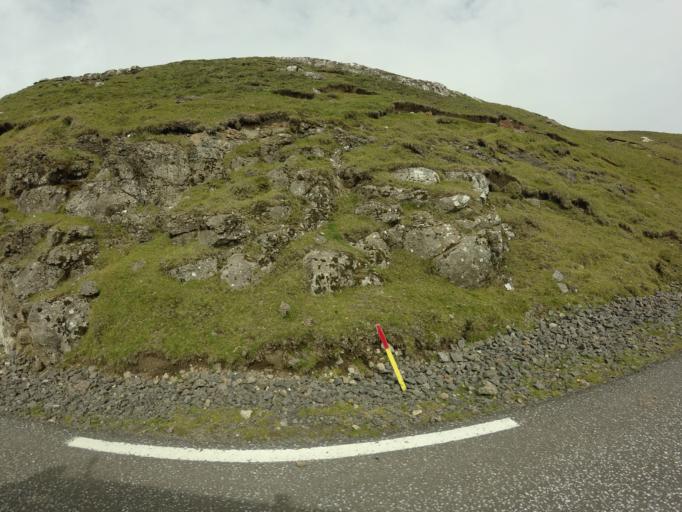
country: FO
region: Sandoy
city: Sandur
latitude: 61.8267
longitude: -6.7485
